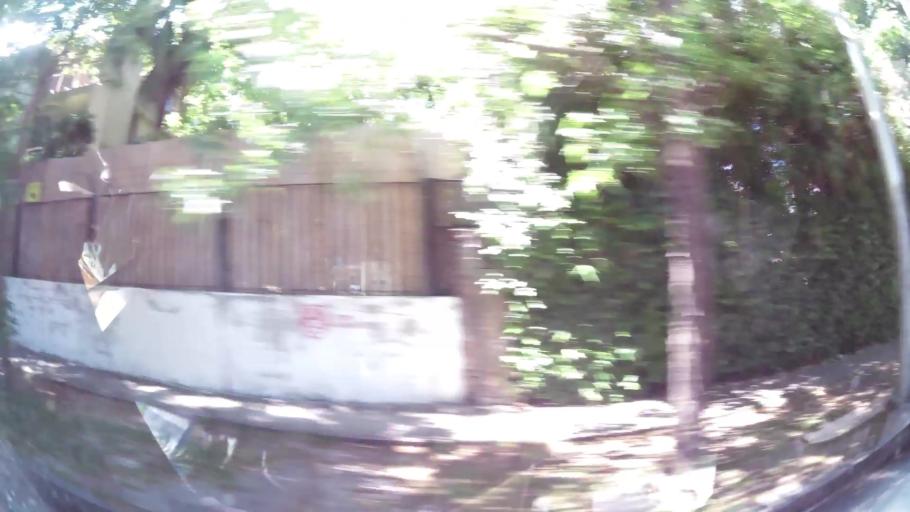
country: AR
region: Buenos Aires
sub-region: Partido de Tigre
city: Tigre
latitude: -34.4235
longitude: -58.5890
